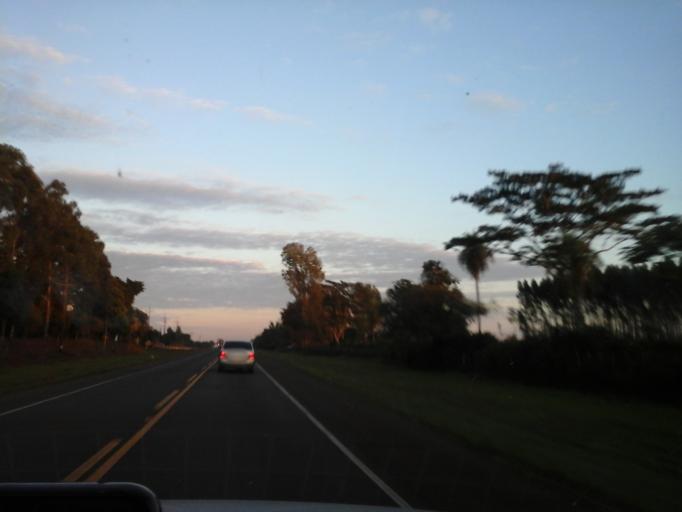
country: PY
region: Itapua
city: General Delgado
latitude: -27.0850
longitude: -56.5451
